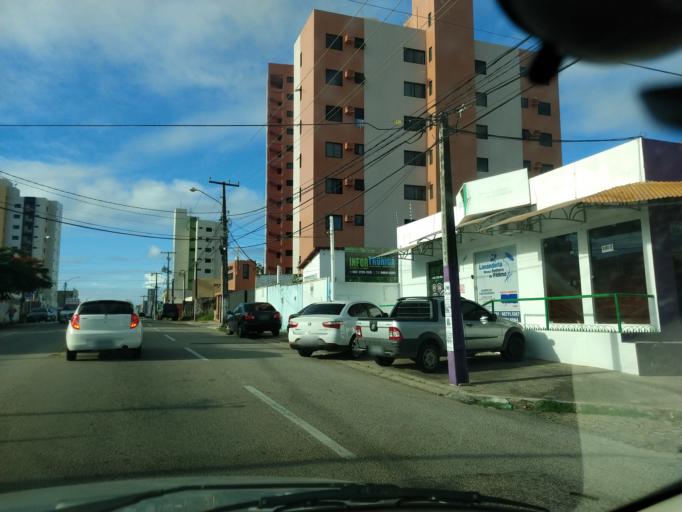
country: BR
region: Rio Grande do Norte
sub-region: Natal
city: Natal
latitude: -5.7973
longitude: -35.2101
